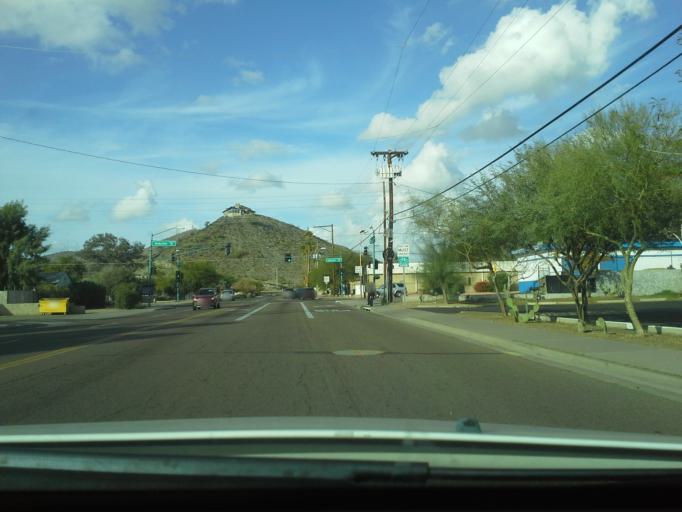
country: US
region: Arizona
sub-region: Maricopa County
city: Glendale
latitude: 33.5704
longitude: -112.0825
